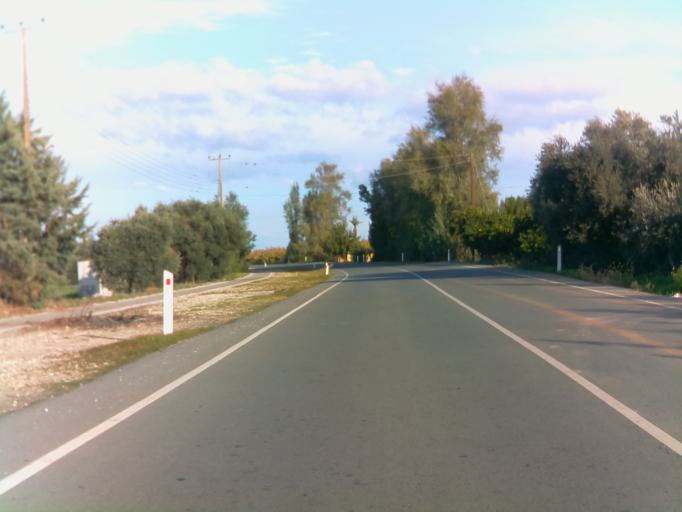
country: CY
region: Pafos
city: Pegeia
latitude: 34.8920
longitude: 32.3358
